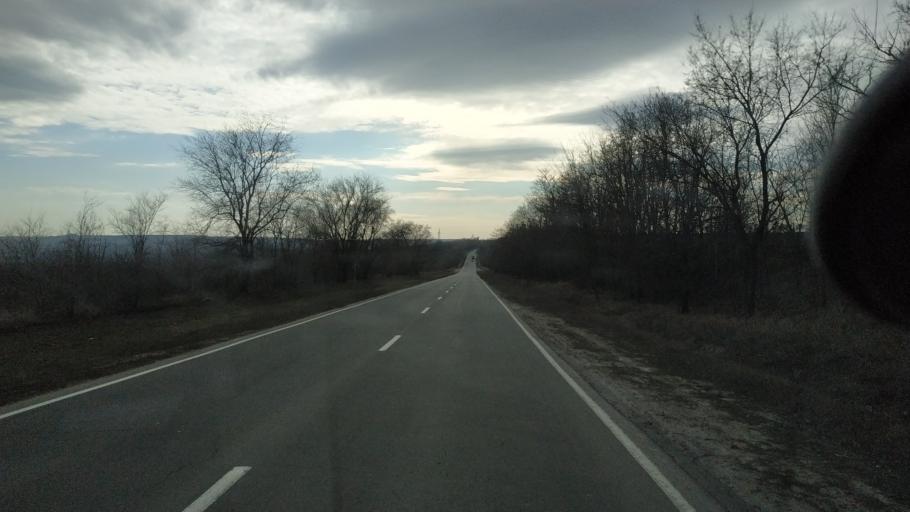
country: MD
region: Chisinau
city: Vadul lui Voda
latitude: 47.0851
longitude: 29.0397
